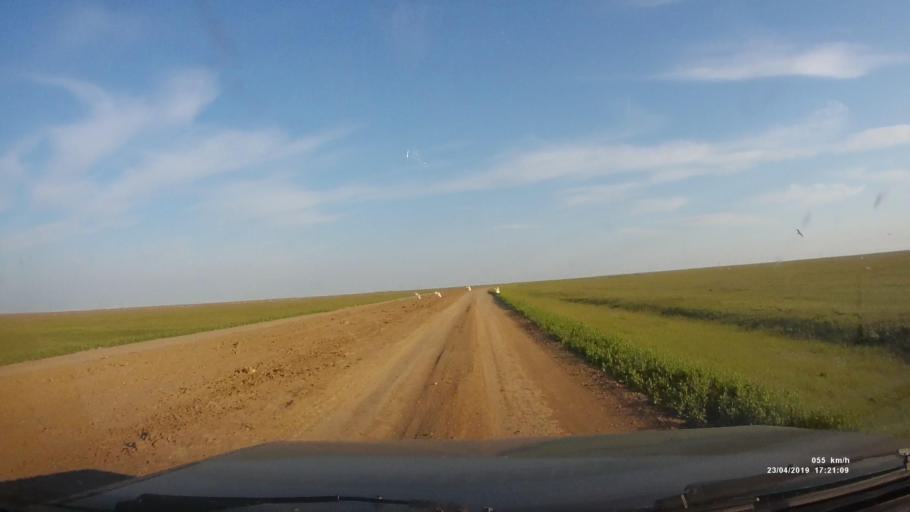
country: RU
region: Kalmykiya
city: Priyutnoye
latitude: 46.1783
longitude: 43.5041
